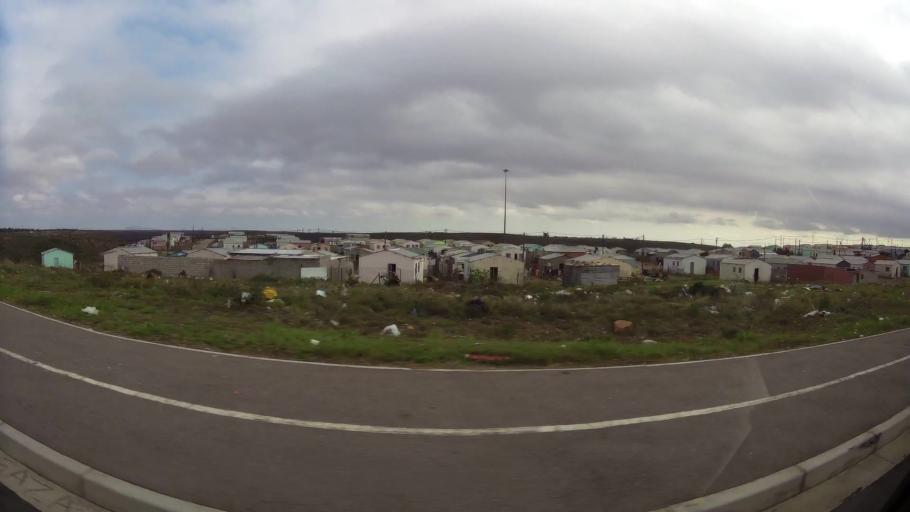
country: ZA
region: Eastern Cape
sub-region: Nelson Mandela Bay Metropolitan Municipality
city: Port Elizabeth
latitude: -33.9150
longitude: 25.5347
